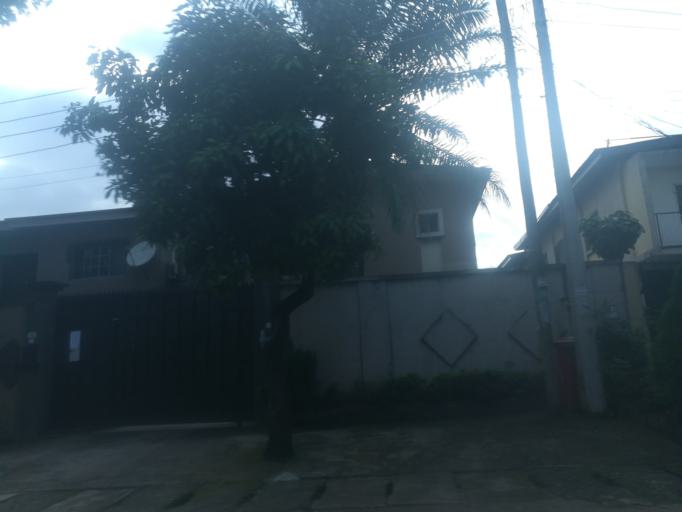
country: NG
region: Lagos
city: Somolu
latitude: 6.5451
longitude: 3.3823
